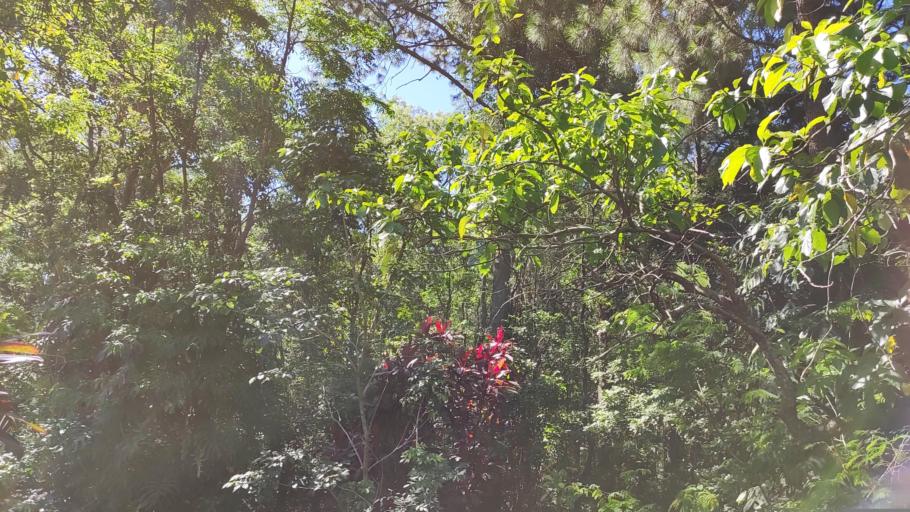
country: AR
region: Misiones
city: Dos de Mayo
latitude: -26.9990
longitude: -54.6283
